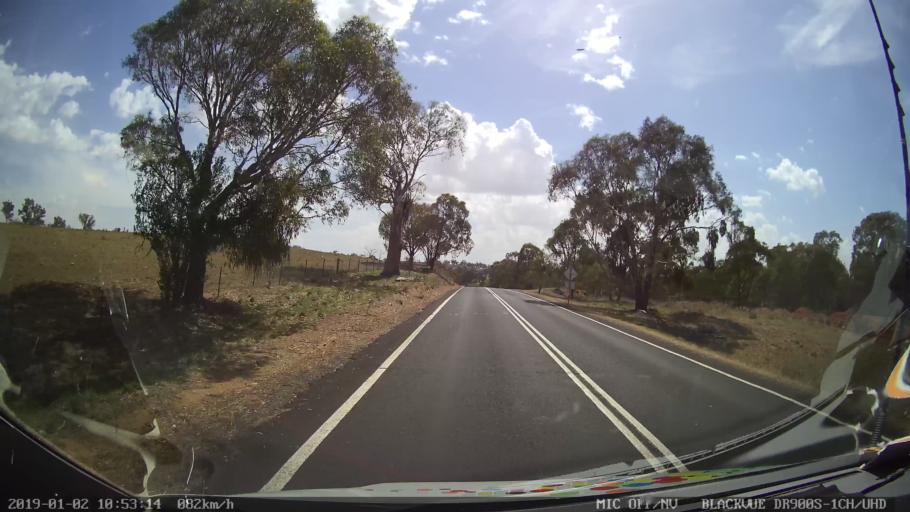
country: AU
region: New South Wales
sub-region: Cootamundra
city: Cootamundra
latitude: -34.6798
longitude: 148.2738
